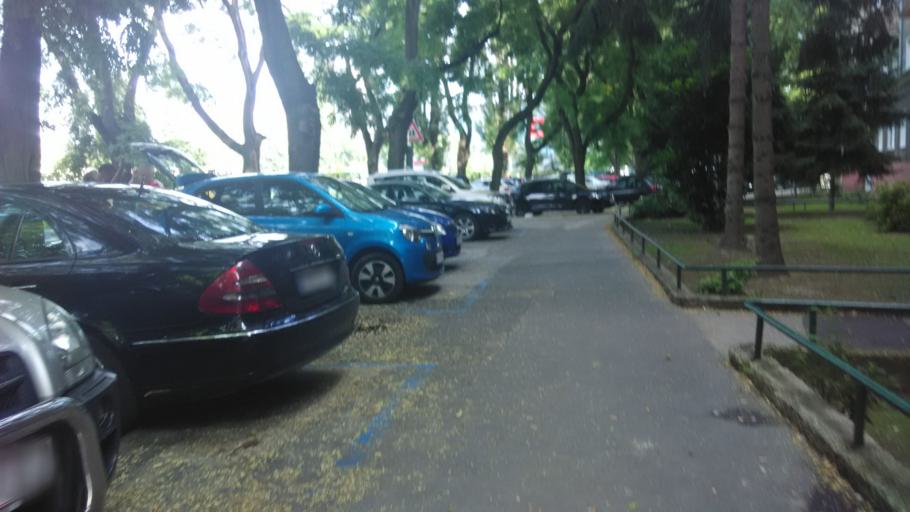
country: SK
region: Bratislavsky
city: Bratislava
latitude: 48.1614
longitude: 17.1335
